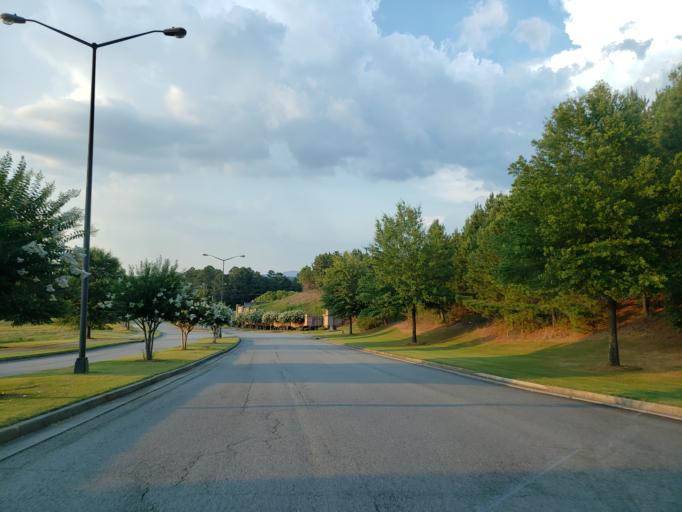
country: US
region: Georgia
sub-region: Bartow County
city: Cartersville
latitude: 34.1150
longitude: -84.8214
